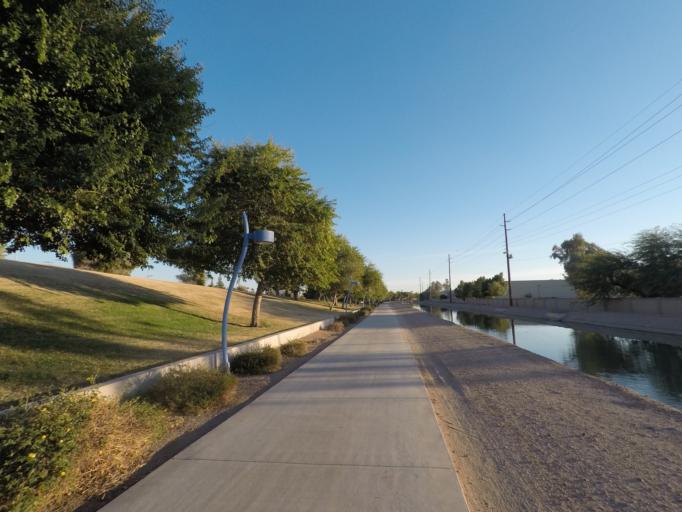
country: US
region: Arizona
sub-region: Maricopa County
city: Guadalupe
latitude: 33.3692
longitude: -111.9390
